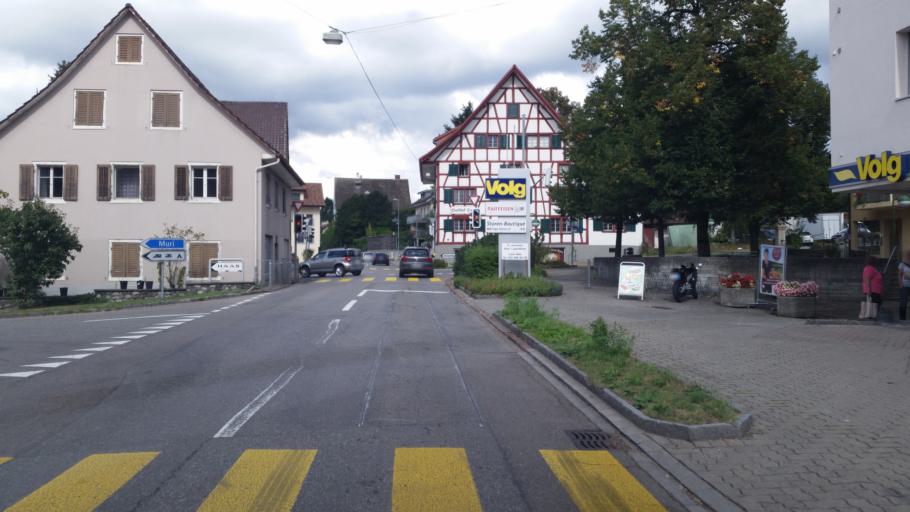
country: CH
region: Zurich
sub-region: Bezirk Affoltern
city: Ottenbach
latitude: 47.2810
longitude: 8.4041
